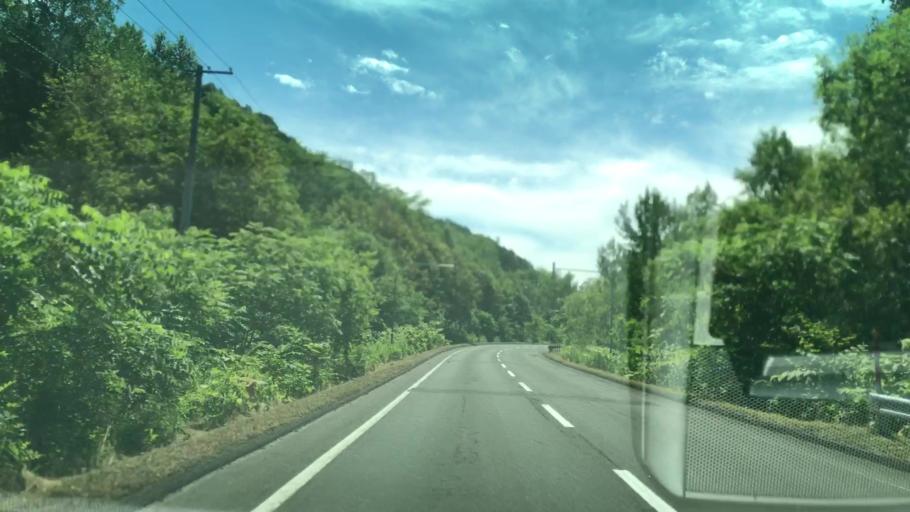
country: JP
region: Hokkaido
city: Shimo-furano
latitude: 42.9685
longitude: 142.4258
